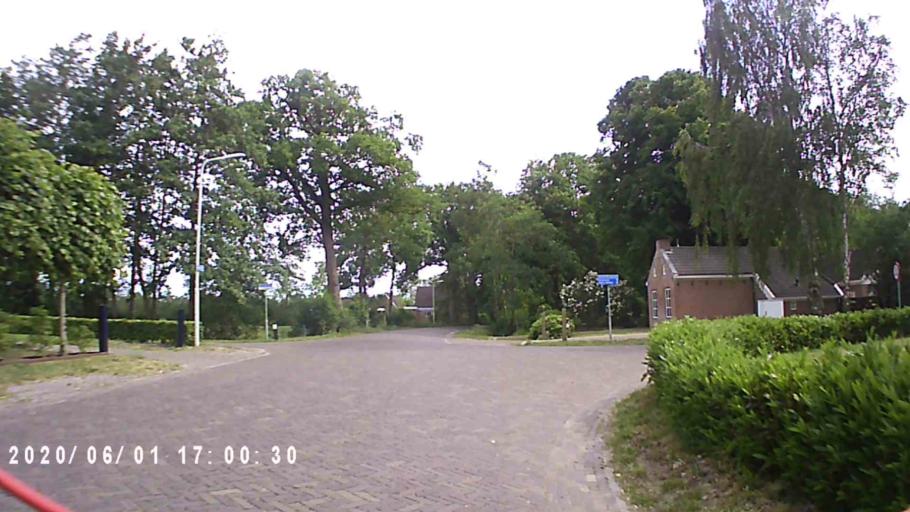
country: NL
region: Friesland
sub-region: Gemeente Tytsjerksteradiel
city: Hurdegaryp
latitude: 53.1829
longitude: 5.9296
